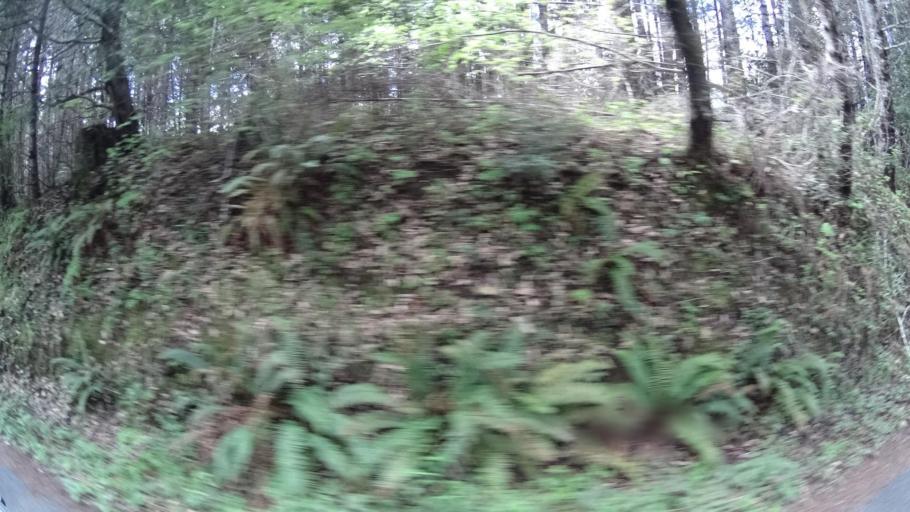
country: US
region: California
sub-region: Humboldt County
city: Blue Lake
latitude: 40.7881
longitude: -123.8810
